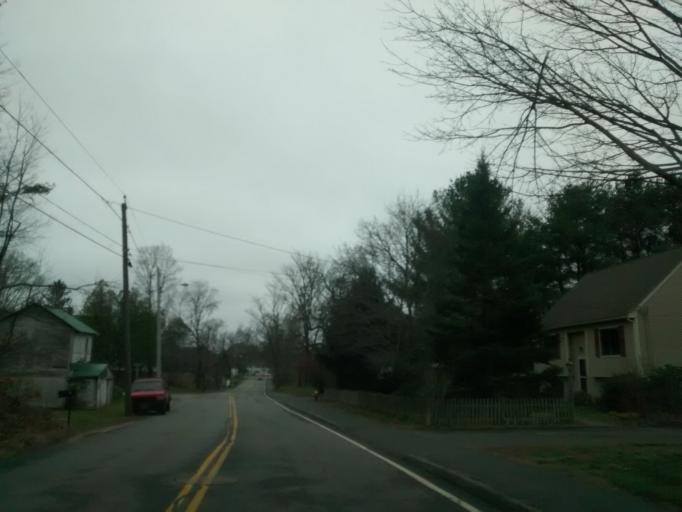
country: US
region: Massachusetts
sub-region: Worcester County
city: Upton
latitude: 42.1730
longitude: -71.6060
